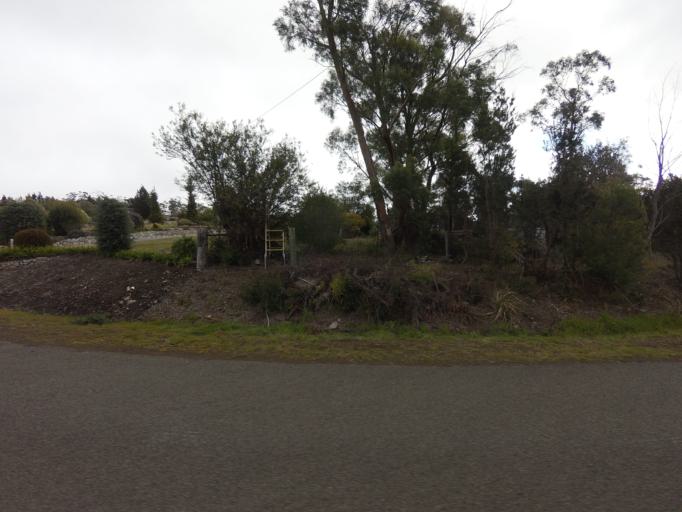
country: AU
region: Tasmania
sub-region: Sorell
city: Sorell
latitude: -42.5345
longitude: 147.9126
